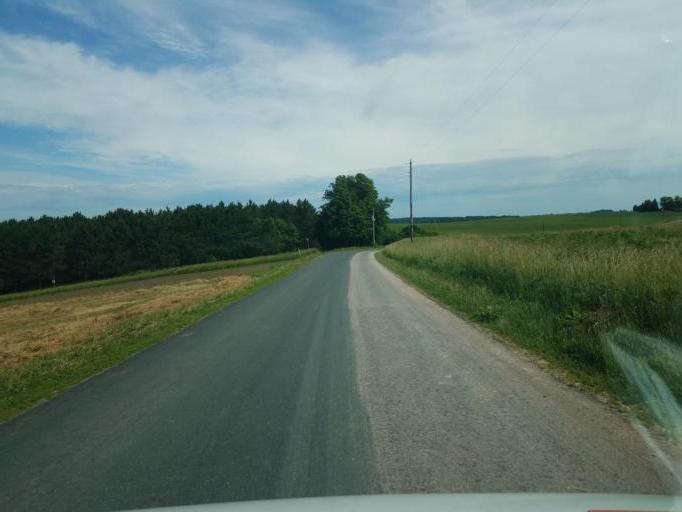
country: US
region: Wisconsin
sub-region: Vernon County
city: Hillsboro
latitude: 43.5583
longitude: -90.3807
